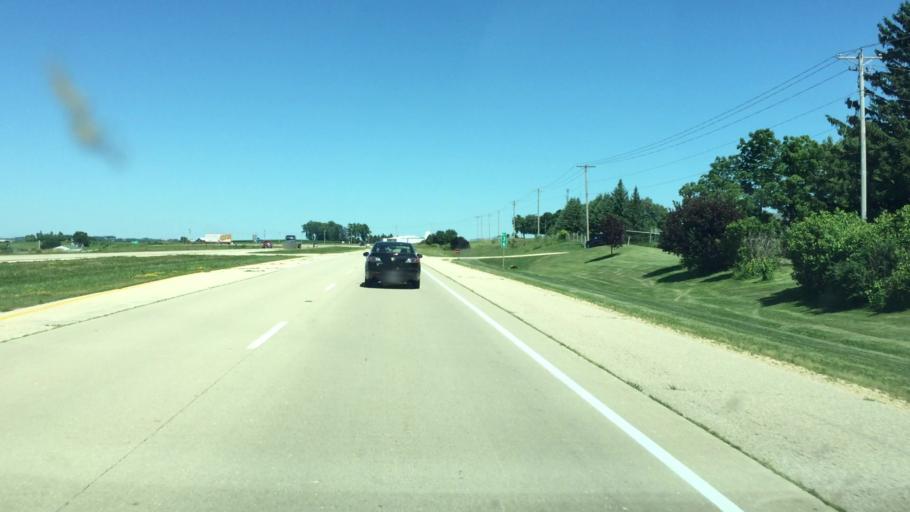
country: US
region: Wisconsin
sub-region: Iowa County
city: Mineral Point
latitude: 42.8403
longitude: -90.2114
